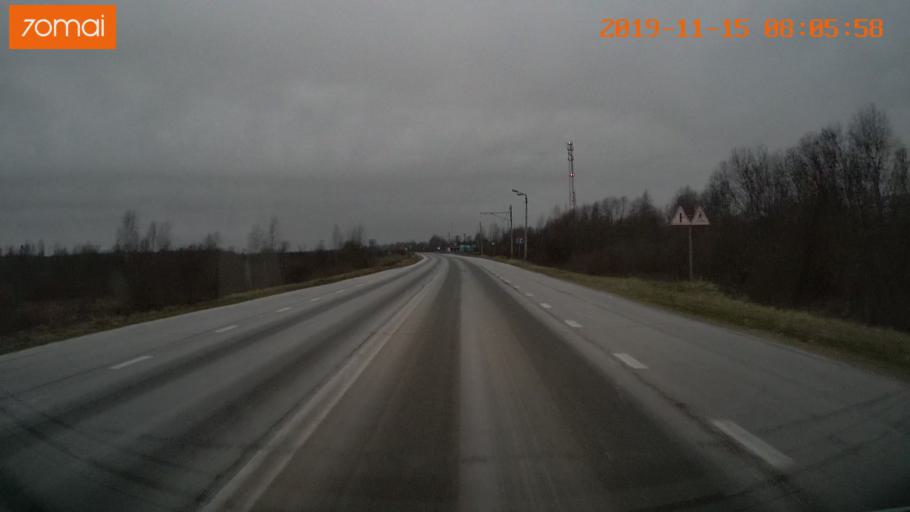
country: RU
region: Vologda
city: Cherepovets
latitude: 59.0200
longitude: 38.0468
